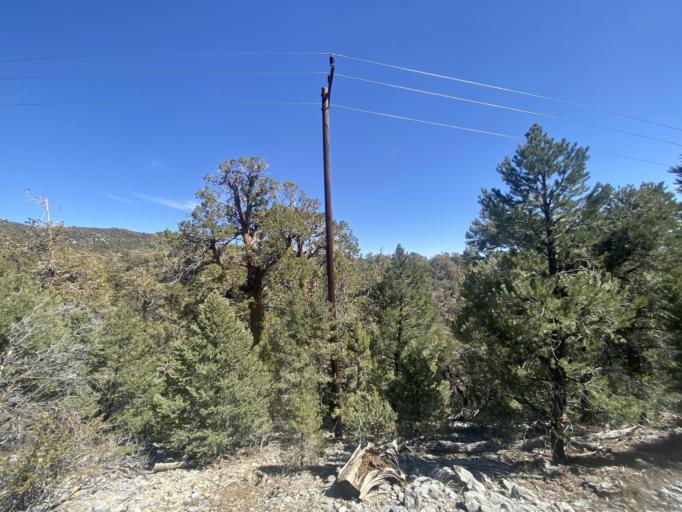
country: US
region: California
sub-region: San Bernardino County
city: Big Bear Lake
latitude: 34.3180
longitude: -116.9273
